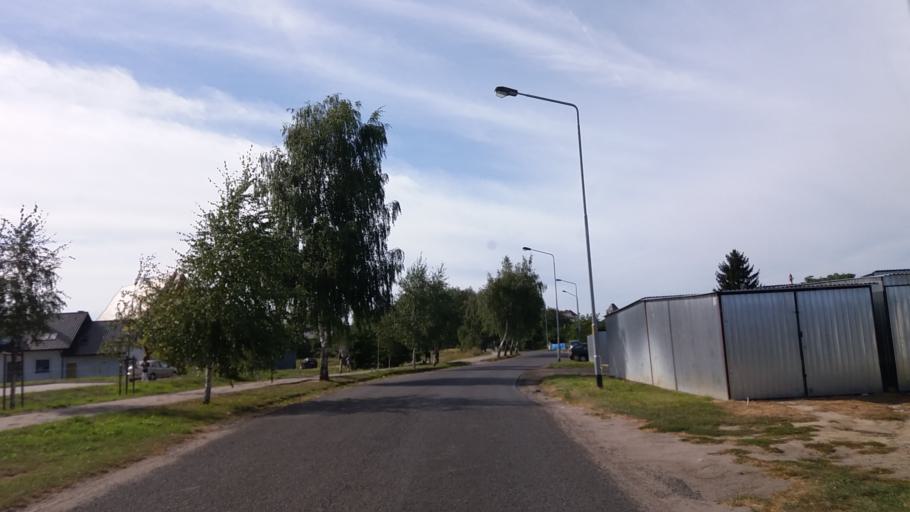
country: PL
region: West Pomeranian Voivodeship
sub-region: Powiat choszczenski
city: Choszczno
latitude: 53.1633
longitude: 15.4331
